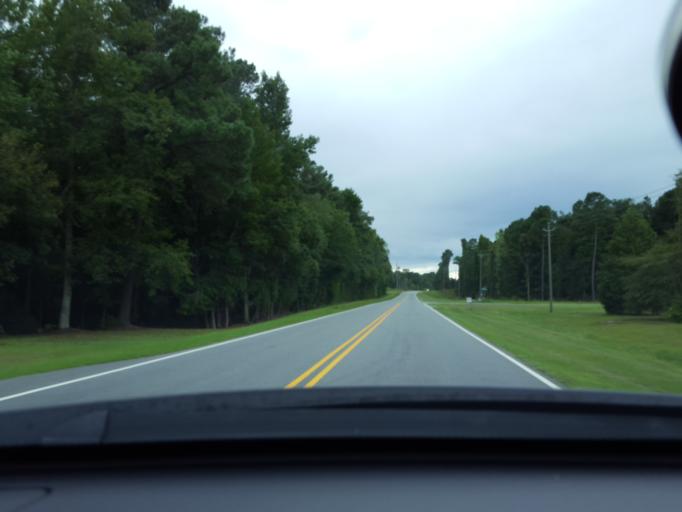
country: US
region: North Carolina
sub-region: Sampson County
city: Roseboro
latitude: 34.7540
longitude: -78.4174
